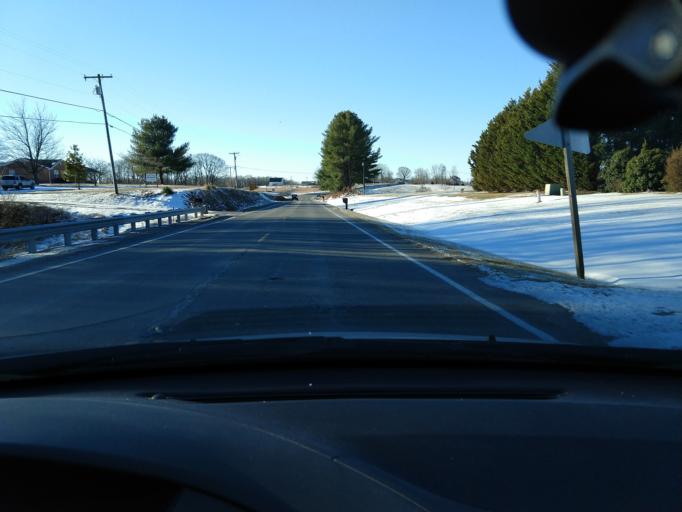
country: US
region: Virginia
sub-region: City of Bedford
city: Bedford
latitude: 37.2992
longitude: -79.5374
